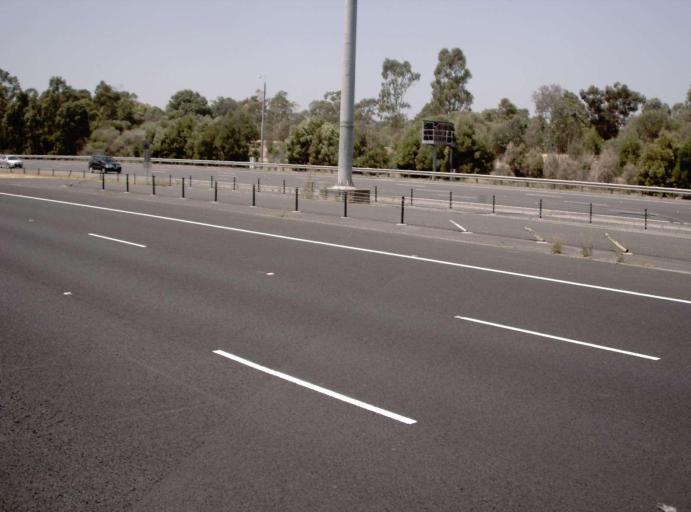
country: AU
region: Victoria
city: Ivanhoe East
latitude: -37.7842
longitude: 145.0661
